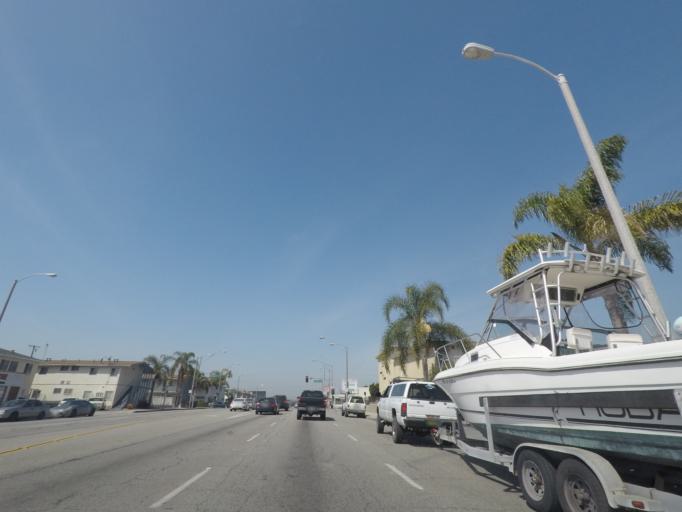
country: US
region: California
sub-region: Los Angeles County
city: Hawthorne
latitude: 33.9165
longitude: -118.3562
